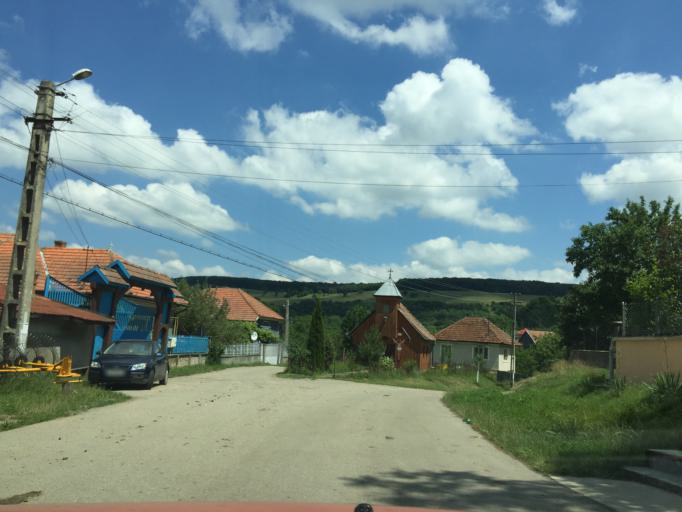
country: RO
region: Cluj
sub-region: Comuna Baciu
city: Baciu
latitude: 46.8238
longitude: 23.5343
